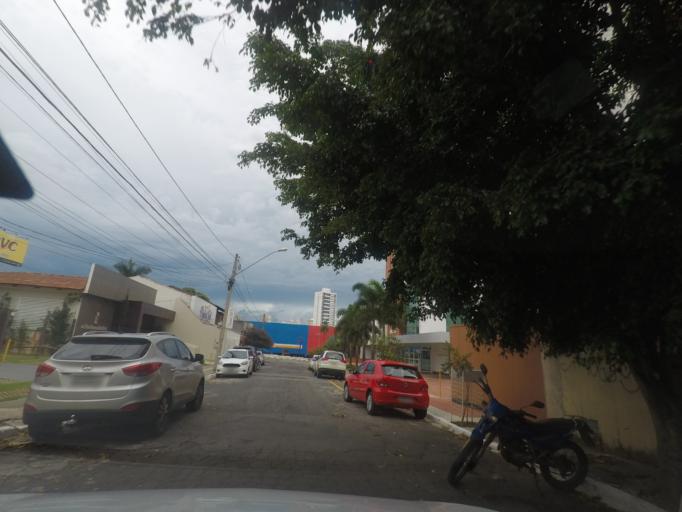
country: BR
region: Goias
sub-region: Goiania
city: Goiania
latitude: -16.6925
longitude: -49.2691
